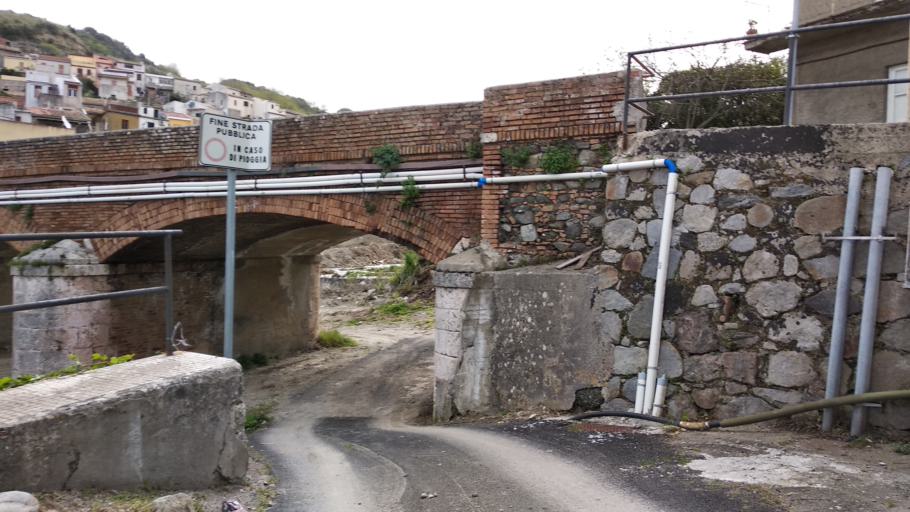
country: IT
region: Sicily
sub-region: Messina
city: Villafranca Tirrena
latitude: 38.2218
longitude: 15.4529
